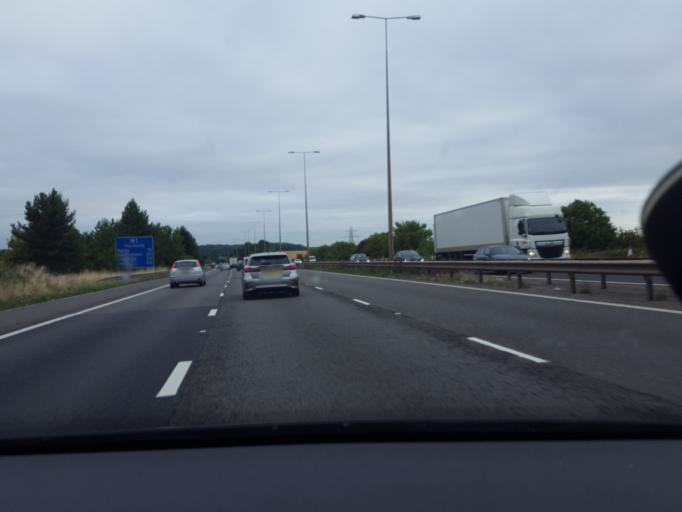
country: GB
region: England
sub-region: Leicestershire
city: Shepshed
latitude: 52.7677
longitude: -1.2753
